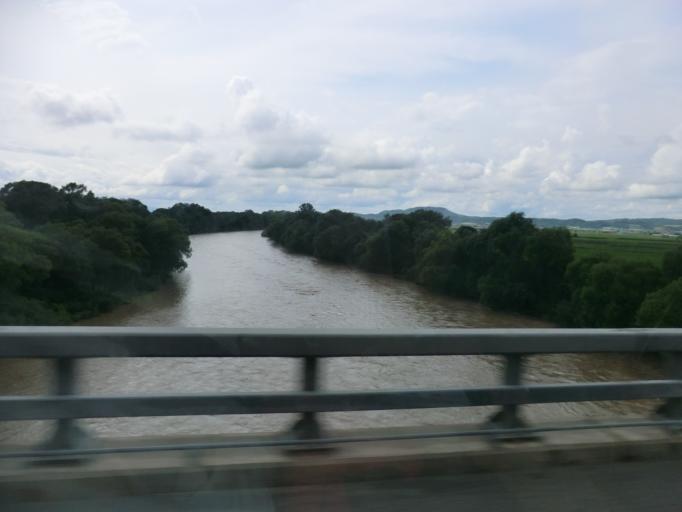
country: JP
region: Hokkaido
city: Fukagawa
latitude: 43.7183
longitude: 142.1649
